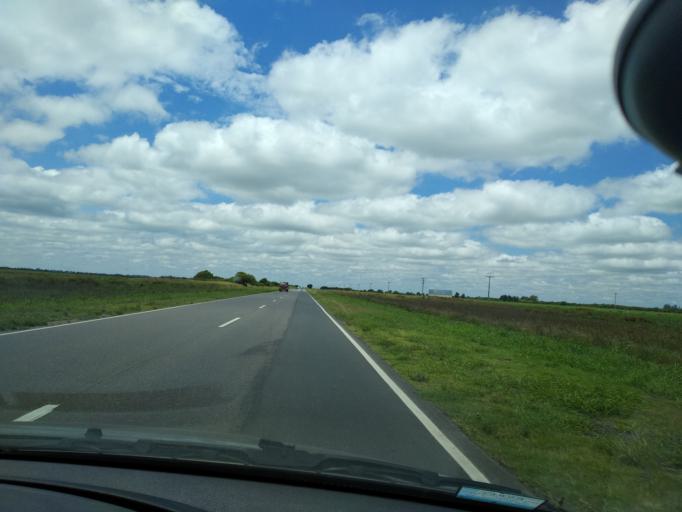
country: AR
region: Cordoba
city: Toledo
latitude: -31.6449
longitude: -64.0052
